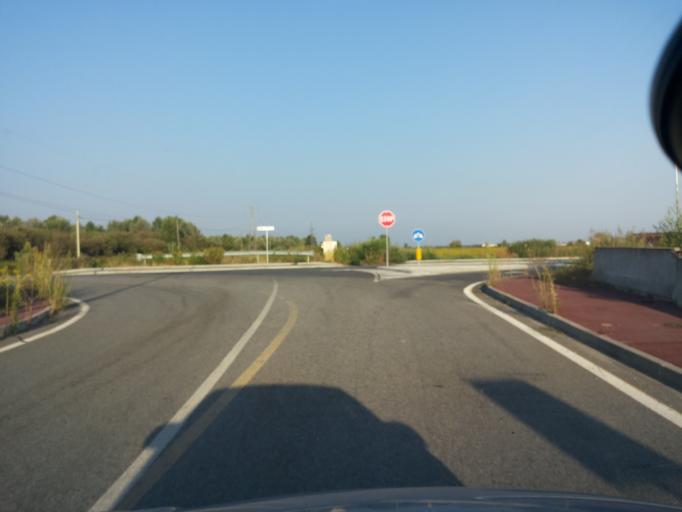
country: IT
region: Piedmont
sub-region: Provincia di Vercelli
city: Vercelli
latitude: 45.2954
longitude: 8.4024
